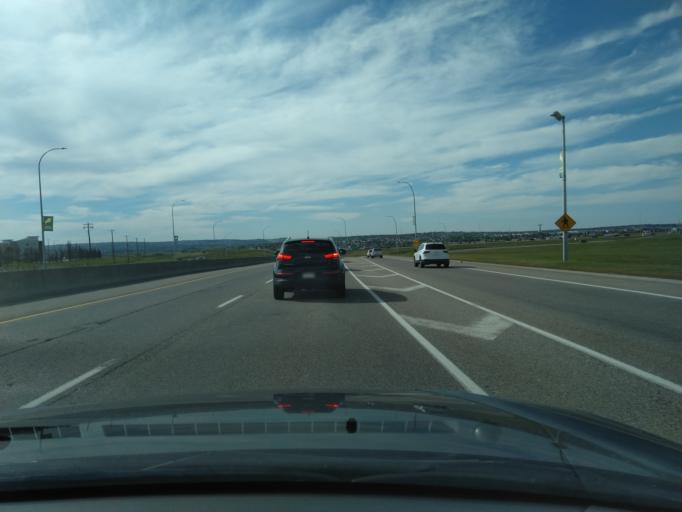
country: CA
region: Alberta
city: Calgary
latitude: 51.1400
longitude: -114.0277
